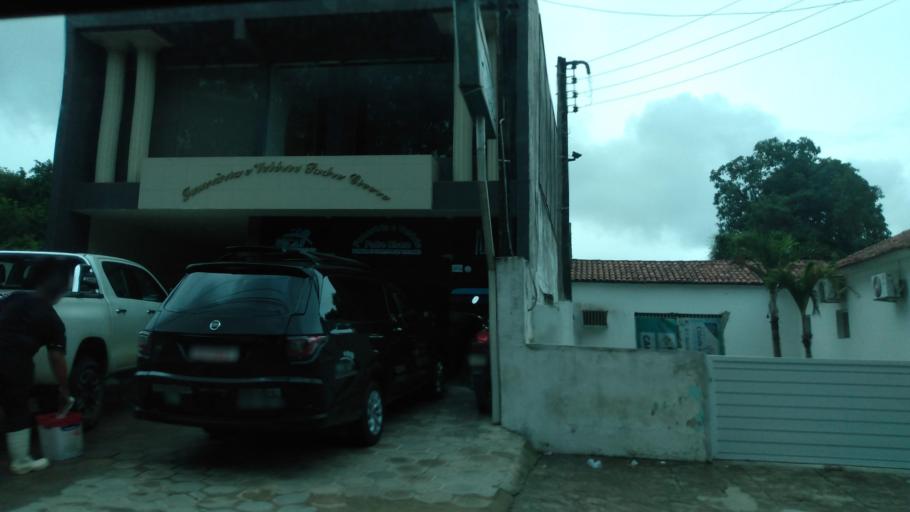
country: BR
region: Pernambuco
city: Garanhuns
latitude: -8.8836
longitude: -36.4834
